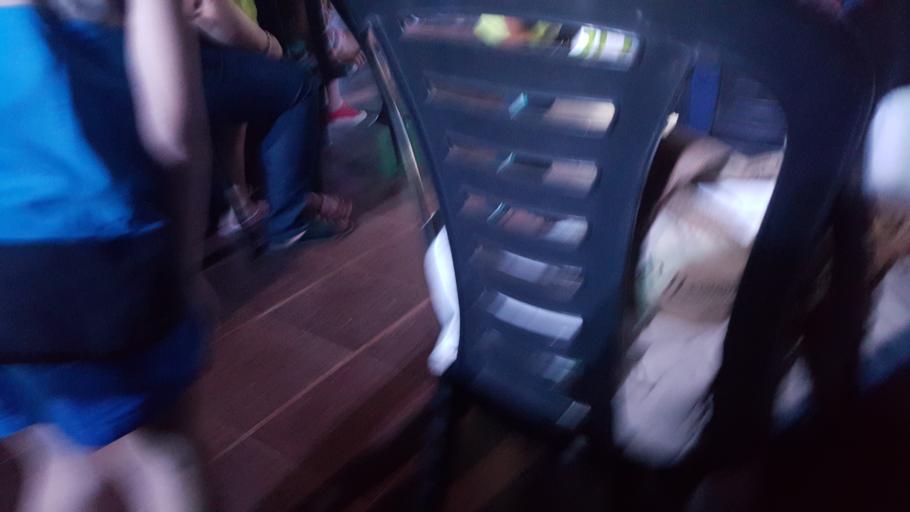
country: AR
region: Misiones
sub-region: Departamento de Capital
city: Posadas
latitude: -27.3647
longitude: -55.9272
